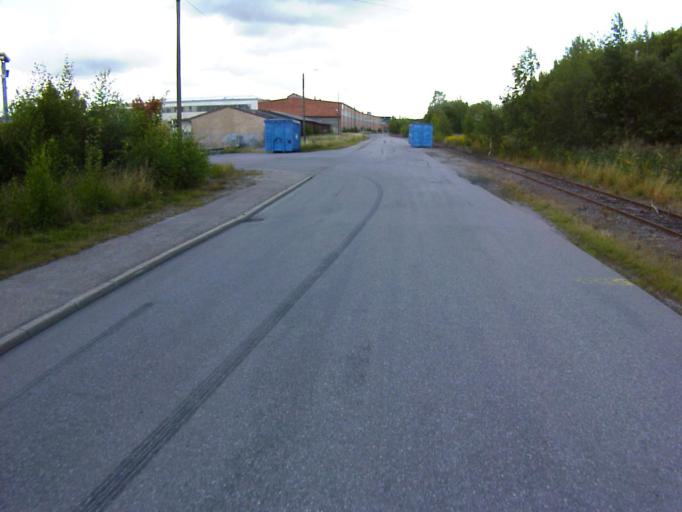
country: SE
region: Soedermanland
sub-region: Eskilstuna Kommun
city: Eskilstuna
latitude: 59.3793
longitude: 16.4832
